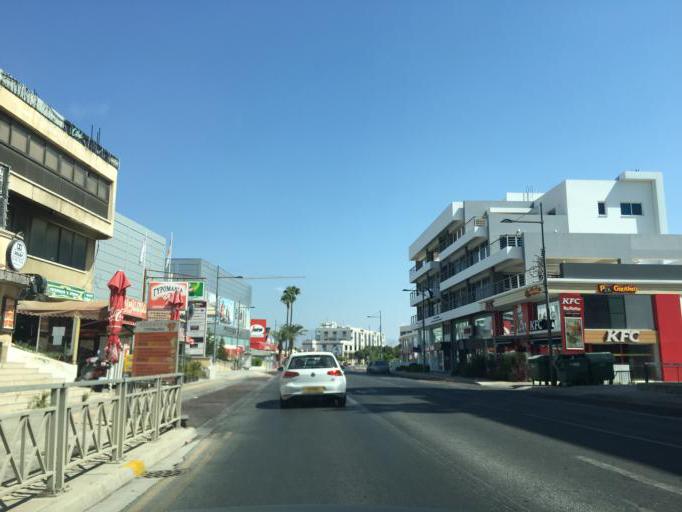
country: CY
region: Lefkosia
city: Nicosia
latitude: 35.1623
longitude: 33.3175
